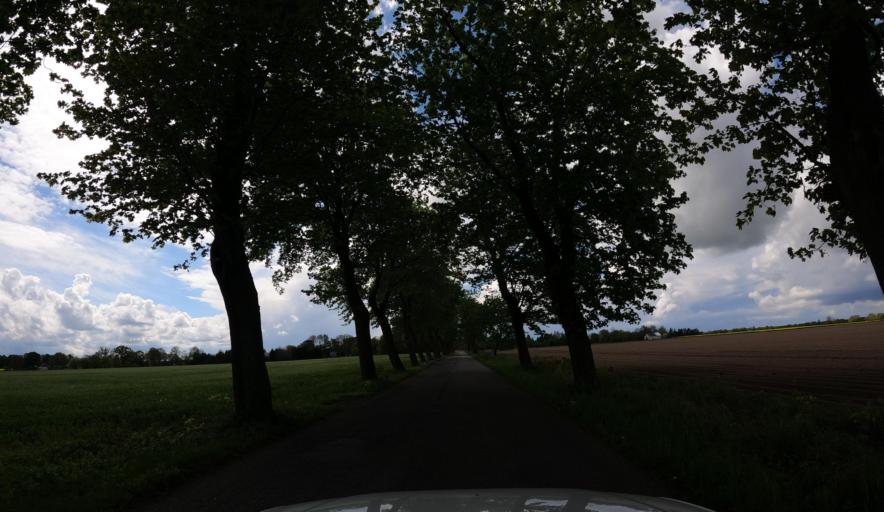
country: PL
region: West Pomeranian Voivodeship
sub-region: Powiat kamienski
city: Wolin
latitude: 53.8726
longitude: 14.6491
